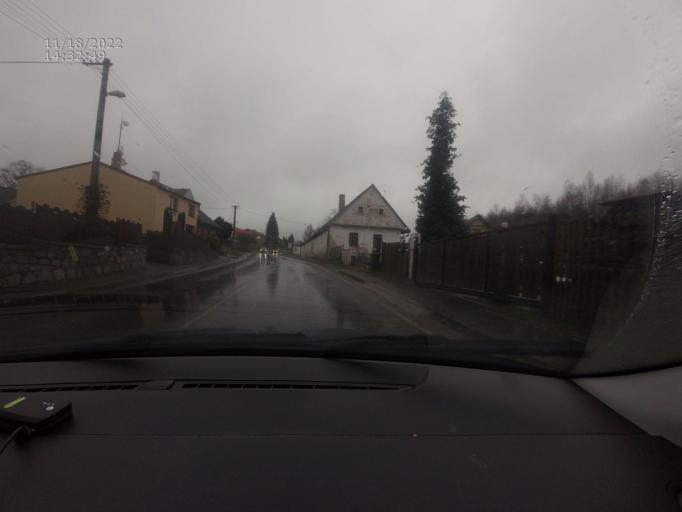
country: CZ
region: Jihocesky
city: Kovarov
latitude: 49.4525
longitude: 14.2867
